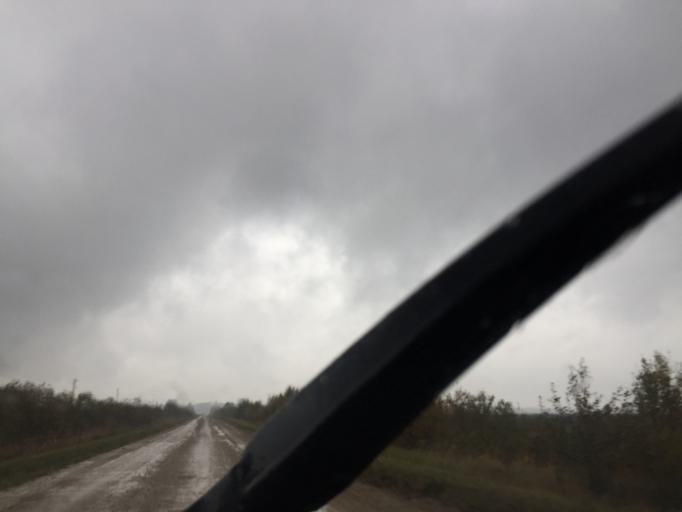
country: LV
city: Tireli
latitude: 56.7248
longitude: 23.5039
